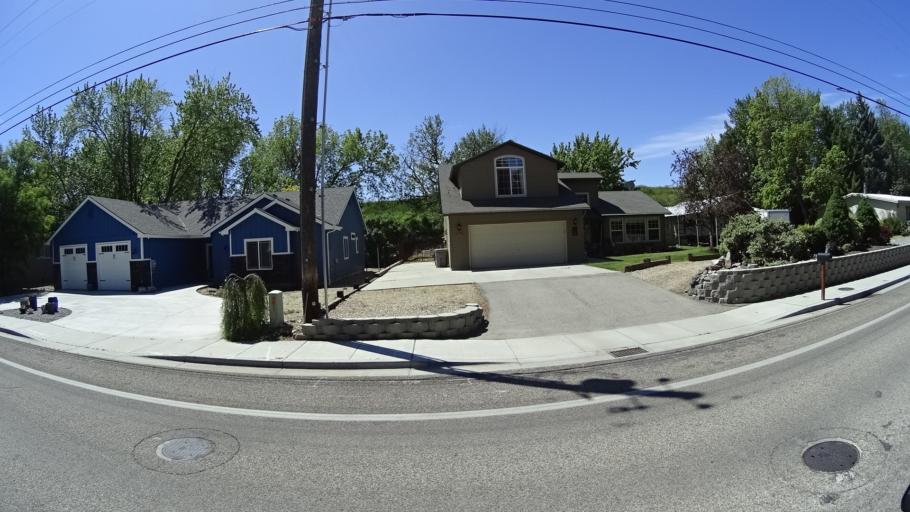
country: US
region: Idaho
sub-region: Ada County
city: Boise
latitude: 43.5642
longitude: -116.1422
